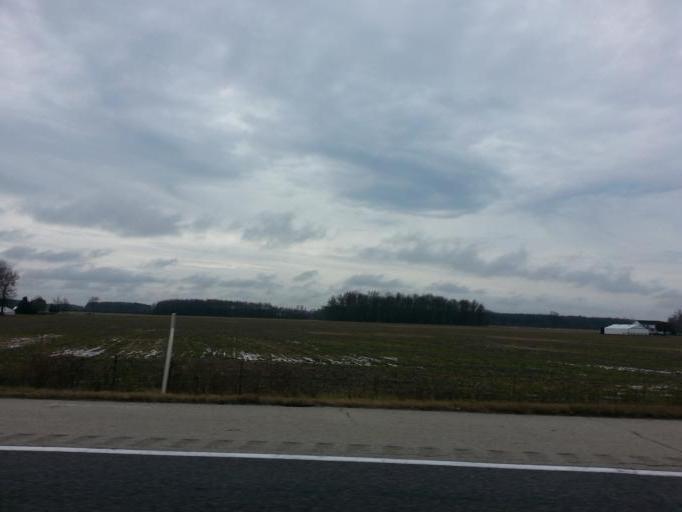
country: US
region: Indiana
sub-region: Ripley County
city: Batesville
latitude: 39.2849
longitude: -85.1571
